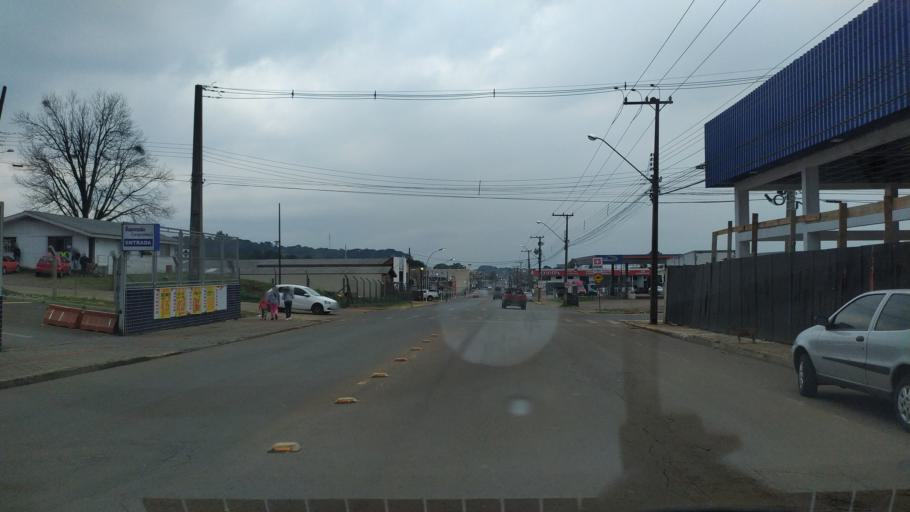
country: BR
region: Parana
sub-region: Palmas
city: Palmas
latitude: -26.4896
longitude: -51.9983
